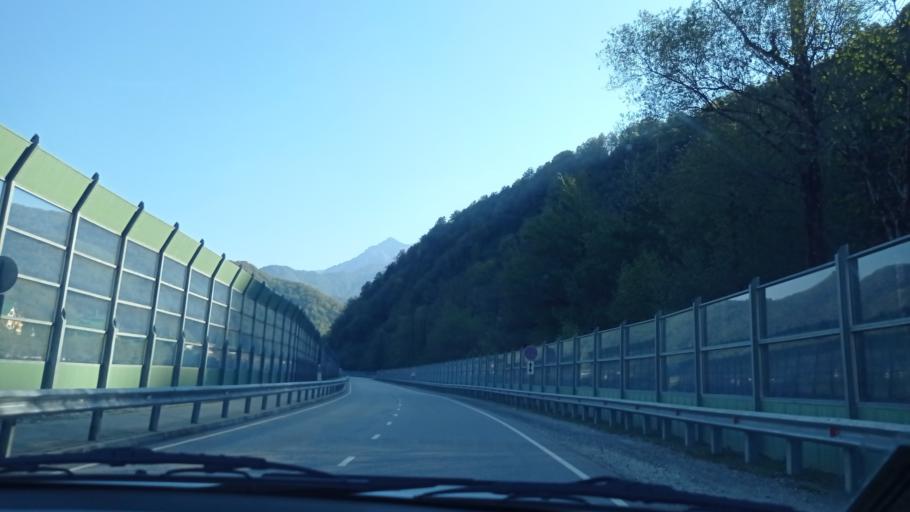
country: RU
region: Krasnodarskiy
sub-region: Sochi City
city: Krasnaya Polyana
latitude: 43.6940
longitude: 40.2692
